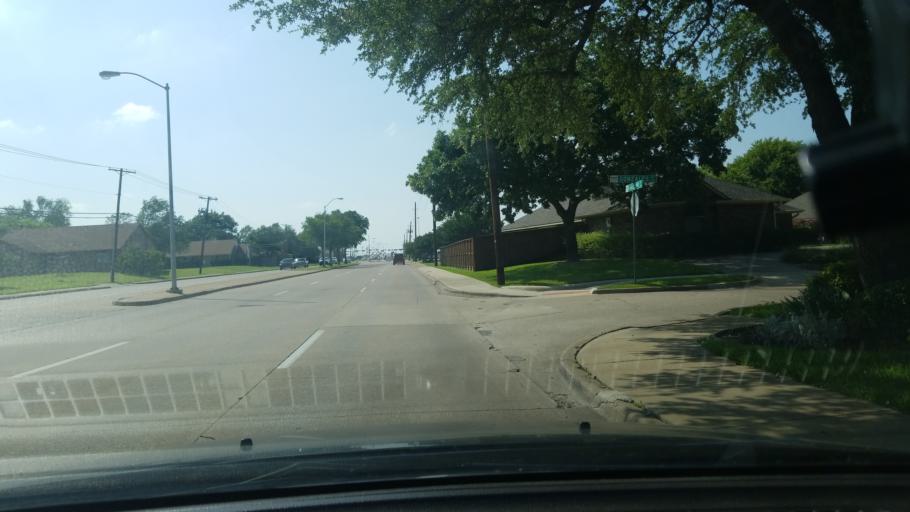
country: US
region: Texas
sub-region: Dallas County
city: Mesquite
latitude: 32.8211
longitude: -96.6188
